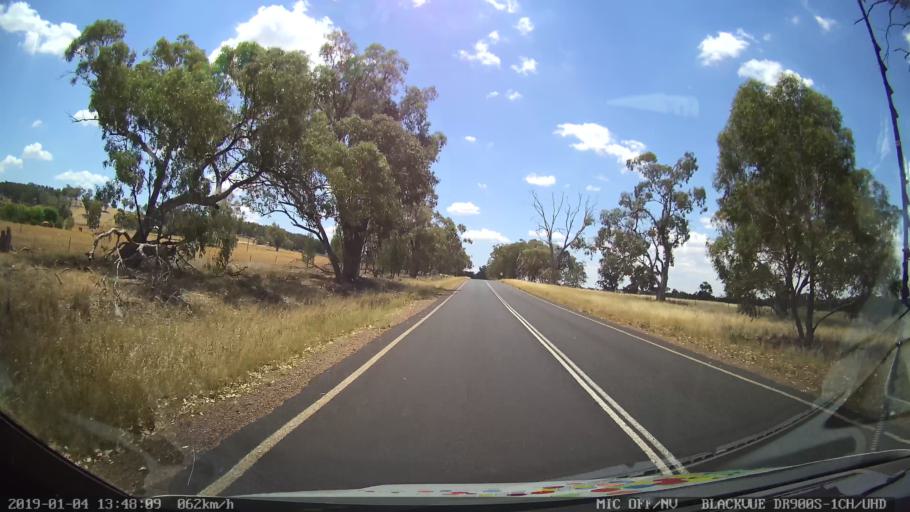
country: AU
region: New South Wales
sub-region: Dubbo Municipality
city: Dubbo
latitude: -32.4455
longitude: 148.5834
